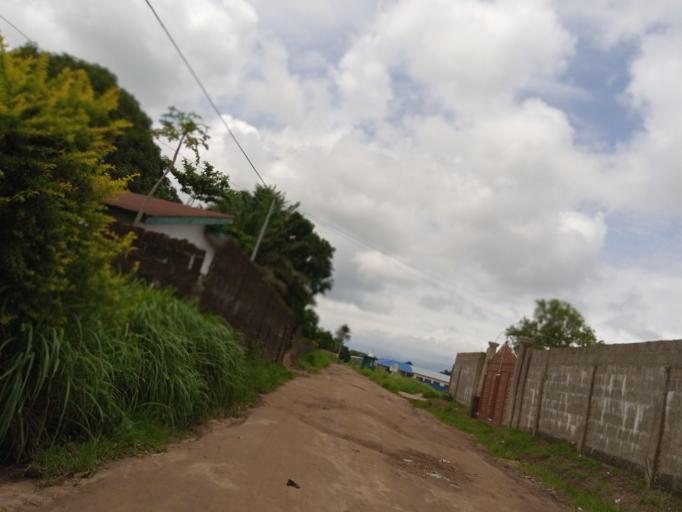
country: SL
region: Northern Province
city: Masoyila
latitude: 8.5995
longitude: -13.1848
